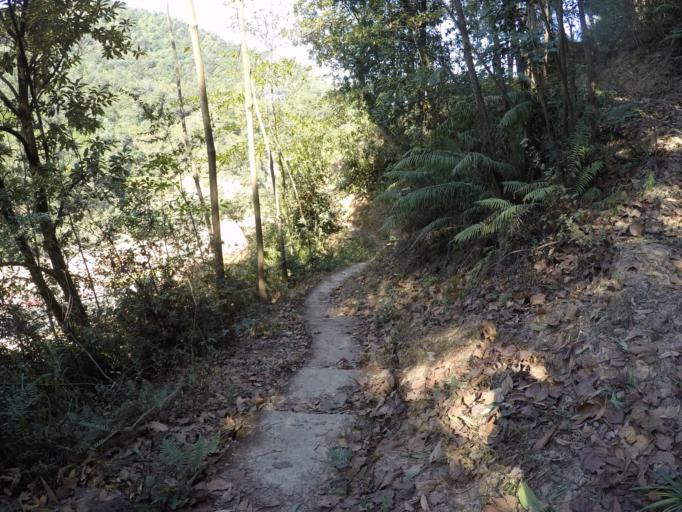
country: CN
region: Guangdong
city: Huancheng
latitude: 22.4641
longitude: 113.4063
